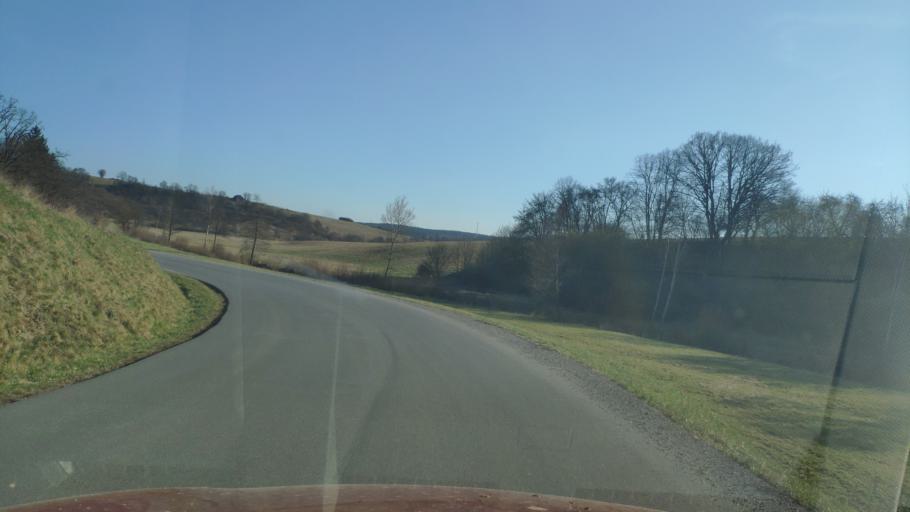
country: SK
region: Banskobystricky
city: Revuca
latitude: 48.5097
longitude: 20.2571
